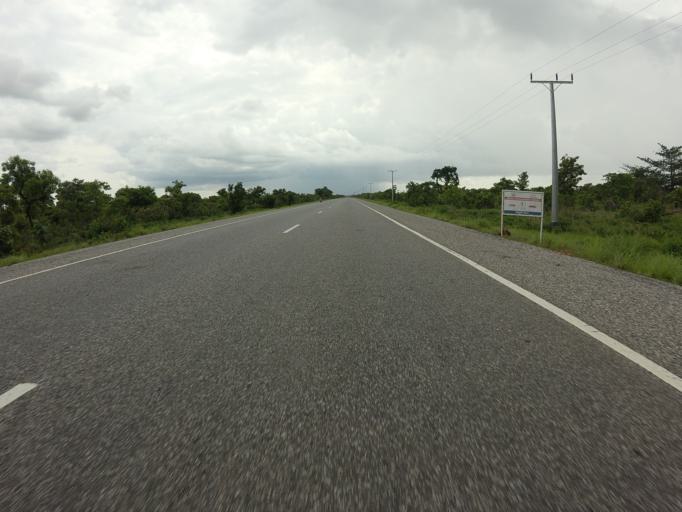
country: GH
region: Northern
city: Tamale
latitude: 9.1311
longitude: -1.3093
